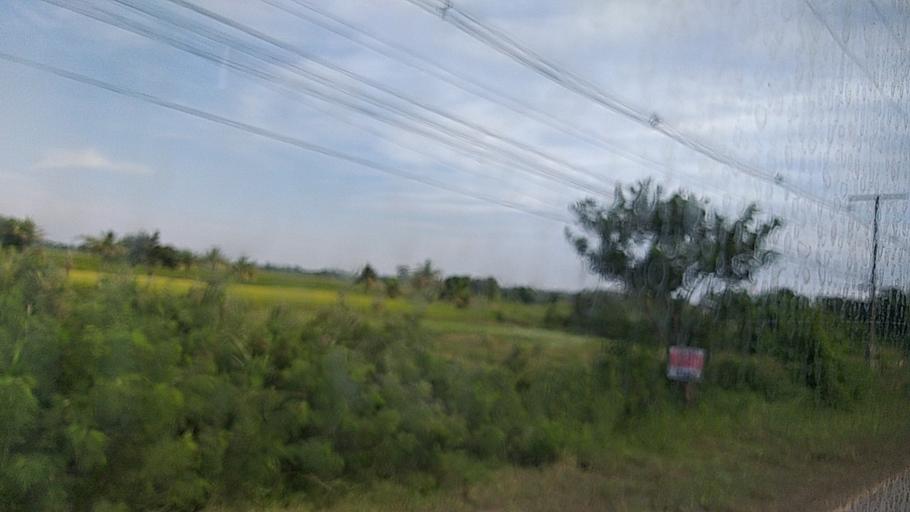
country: TH
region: Maha Sarakham
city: Chiang Yuen
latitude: 16.4424
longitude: 102.9833
